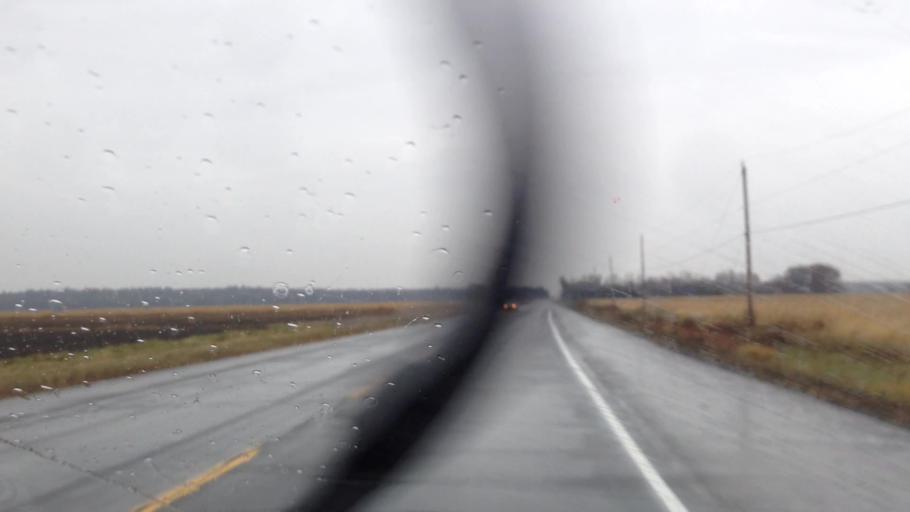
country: CA
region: Ontario
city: Clarence-Rockland
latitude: 45.4469
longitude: -75.4220
